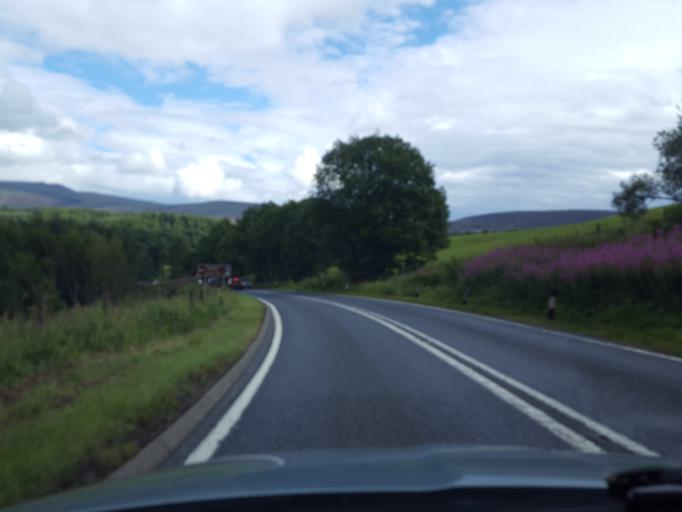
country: GB
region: Scotland
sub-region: Moray
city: Rothes
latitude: 57.4074
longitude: -3.3761
